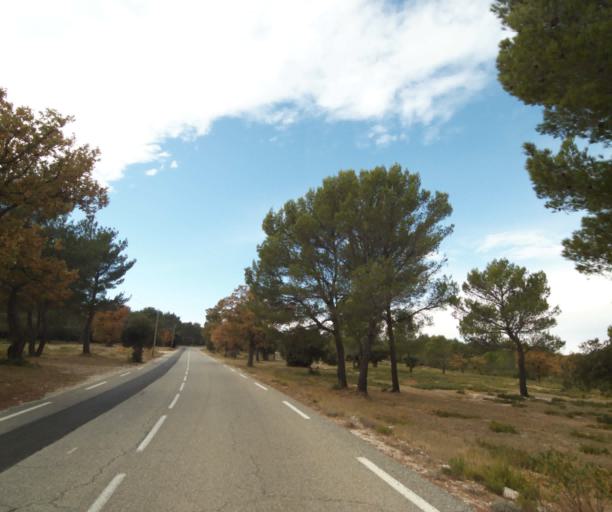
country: FR
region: Provence-Alpes-Cote d'Azur
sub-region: Departement des Bouches-du-Rhone
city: Cuges-les-Pins
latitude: 43.2416
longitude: 5.7008
